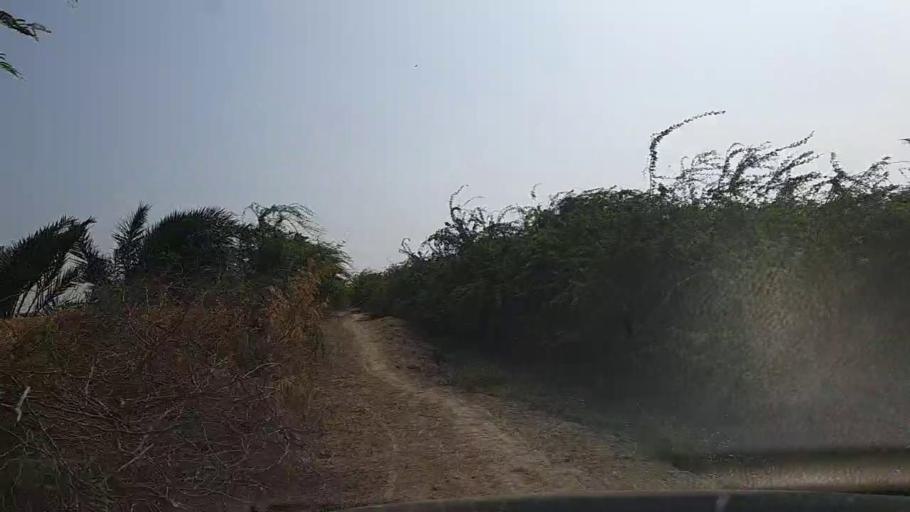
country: PK
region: Sindh
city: Gharo
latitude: 24.7346
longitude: 67.6856
